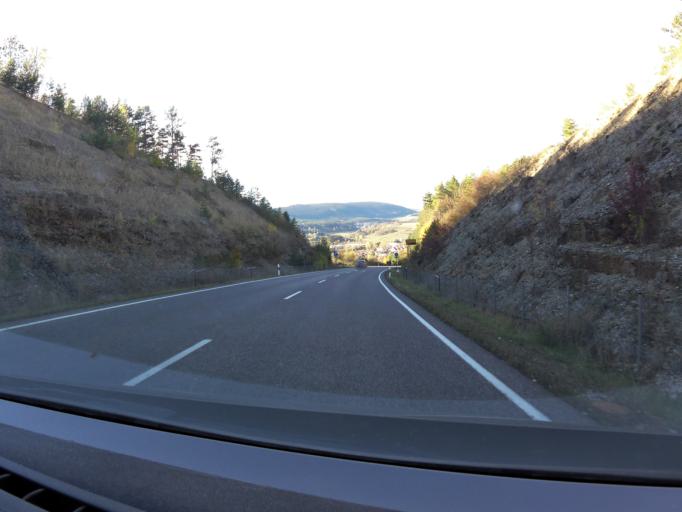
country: DE
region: Thuringia
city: Geschwenda
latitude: 50.7402
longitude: 10.8254
